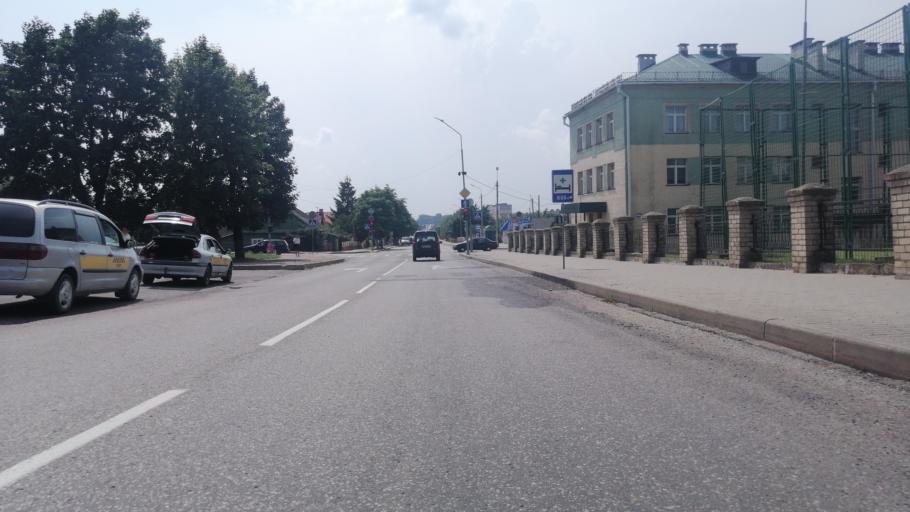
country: BY
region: Grodnenskaya
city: Navahrudak
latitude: 53.5922
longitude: 25.8188
